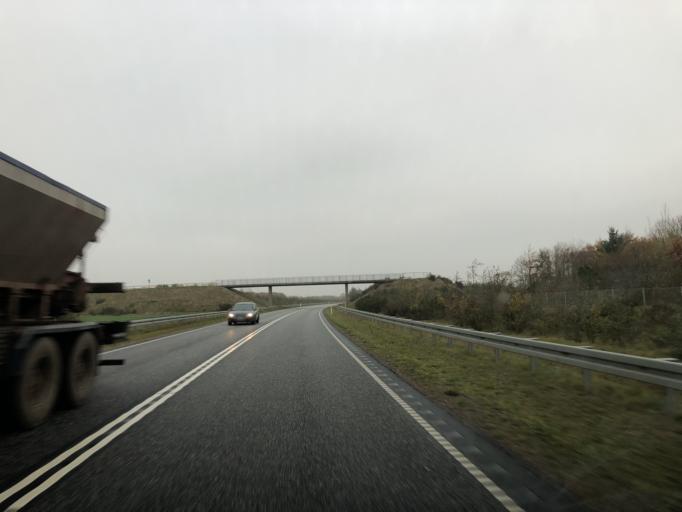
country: DK
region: Central Jutland
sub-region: Herning Kommune
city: Sunds
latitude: 56.2046
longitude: 8.9906
